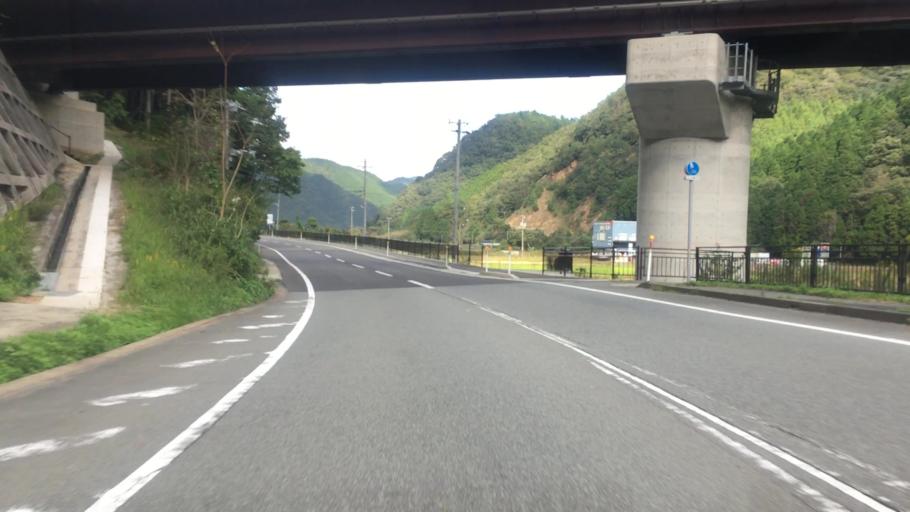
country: JP
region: Hyogo
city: Toyooka
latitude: 35.3628
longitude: 134.7593
